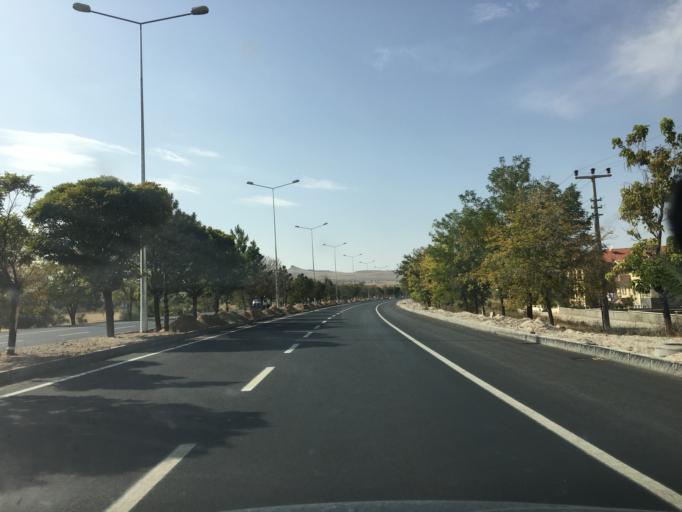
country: TR
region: Nevsehir
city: Avanos
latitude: 38.7038
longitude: 34.8484
